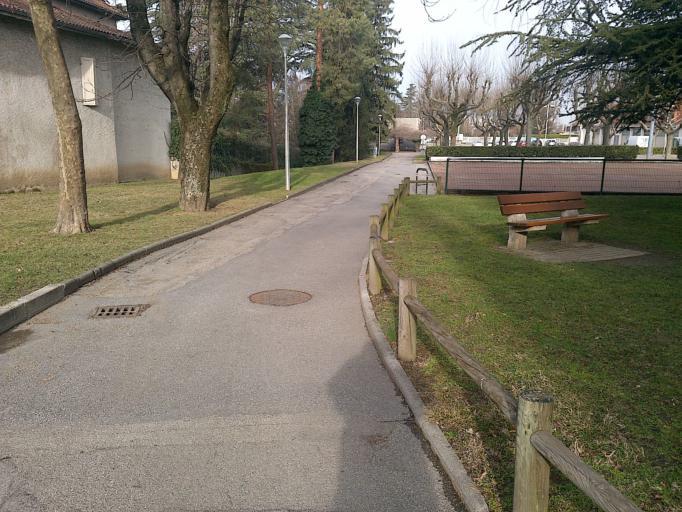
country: FR
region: Rhone-Alpes
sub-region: Departement de l'Isere
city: Eybens
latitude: 45.1477
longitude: 5.7493
